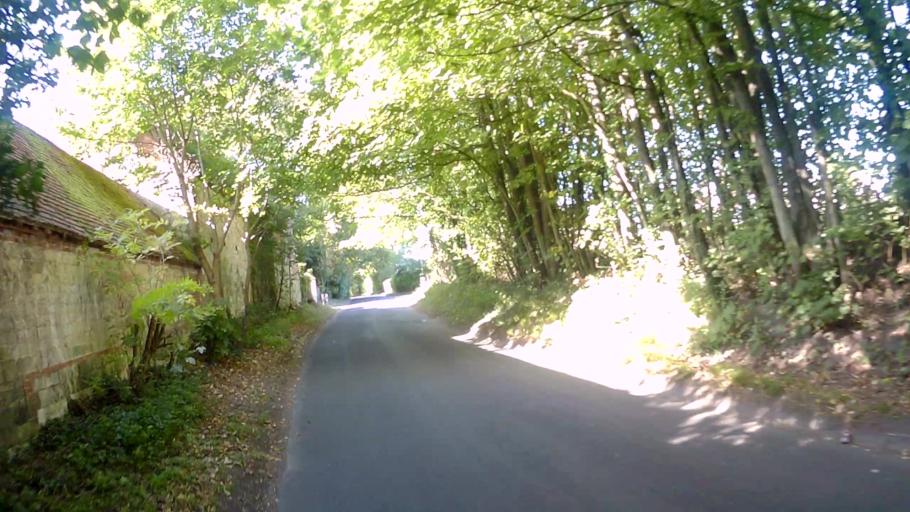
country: GB
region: England
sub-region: Hampshire
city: Long Sutton
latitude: 51.1858
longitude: -0.9005
